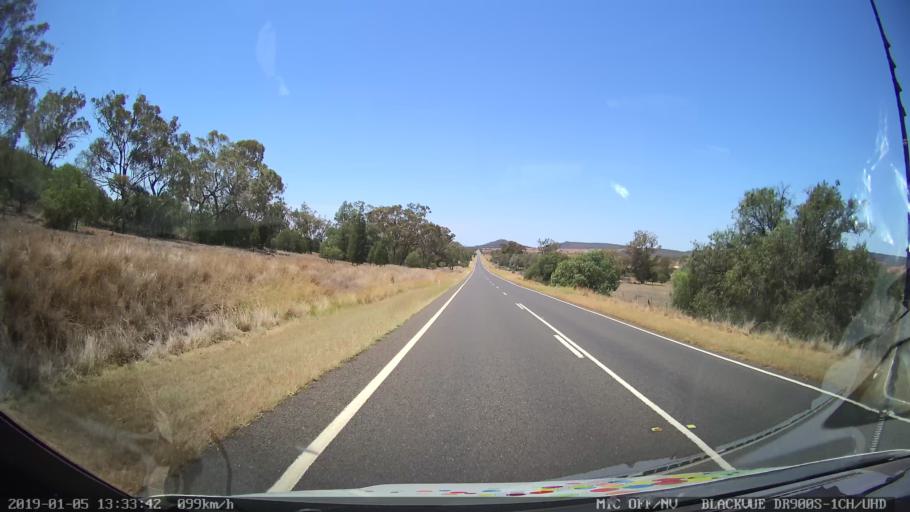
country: AU
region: New South Wales
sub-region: Gunnedah
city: Gunnedah
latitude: -30.9994
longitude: 150.1209
